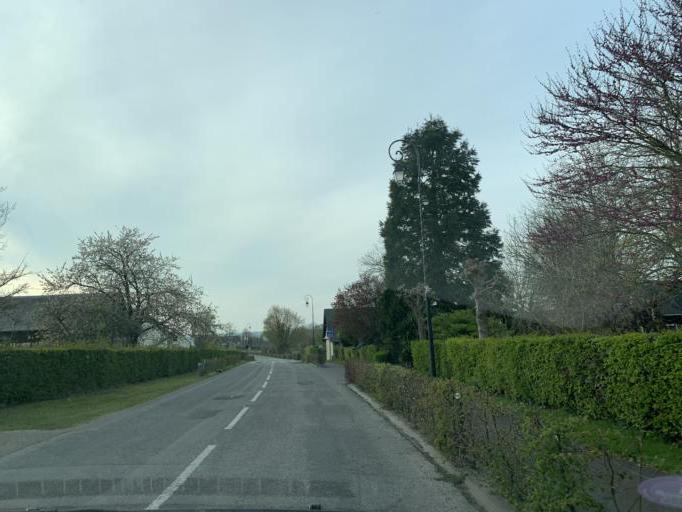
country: FR
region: Haute-Normandie
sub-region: Departement de la Seine-Maritime
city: La Mailleraye-sur-Seine
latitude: 49.4957
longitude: 0.7614
